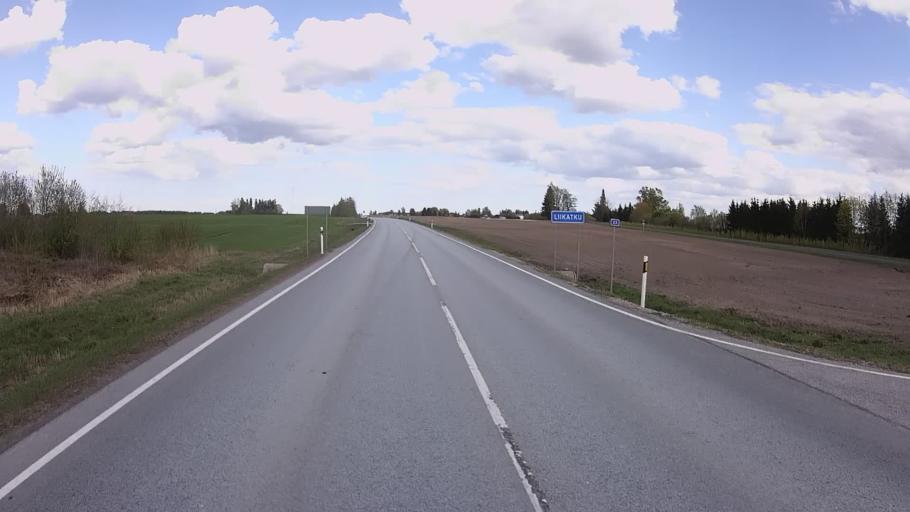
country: EE
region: Jogevamaa
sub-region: Mustvee linn
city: Mustvee
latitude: 58.8231
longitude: 26.6968
